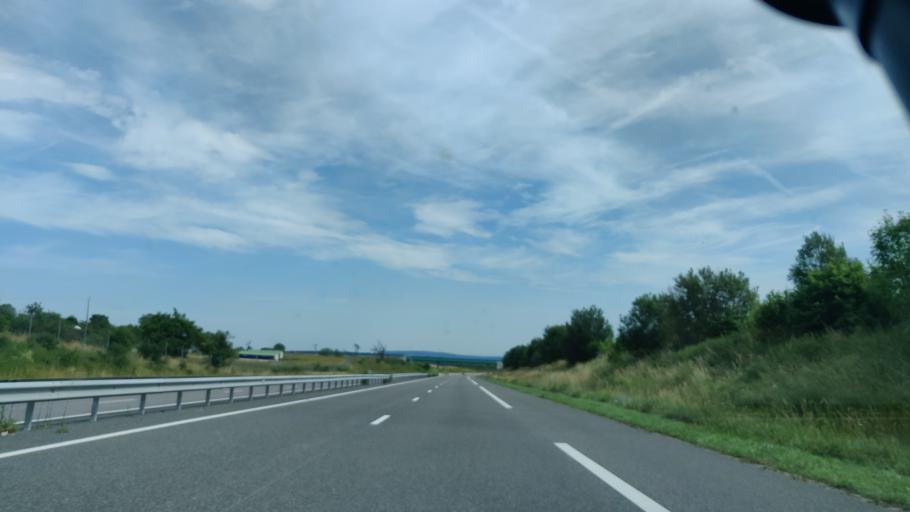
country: FR
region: Lorraine
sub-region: Departement de Meurthe-et-Moselle
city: Baccarat
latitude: 48.4921
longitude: 6.7042
